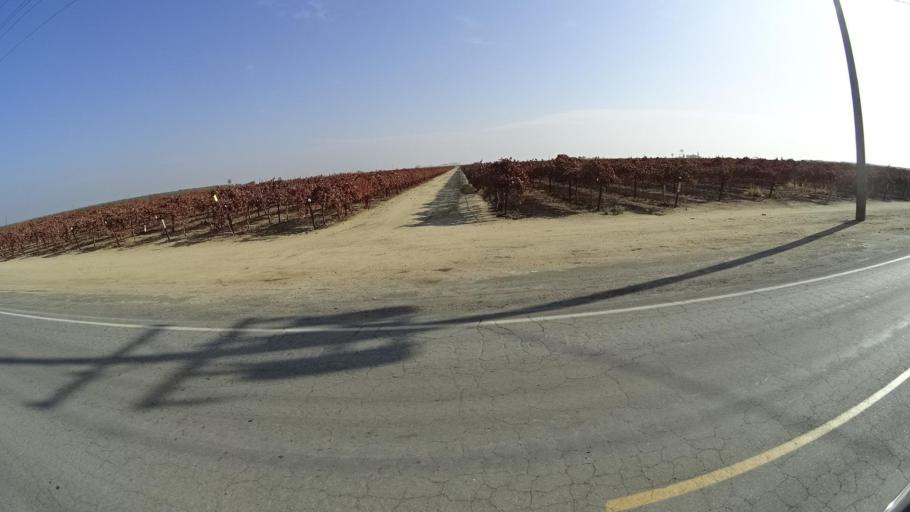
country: US
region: California
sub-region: Kern County
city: Delano
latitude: 35.7434
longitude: -119.2232
